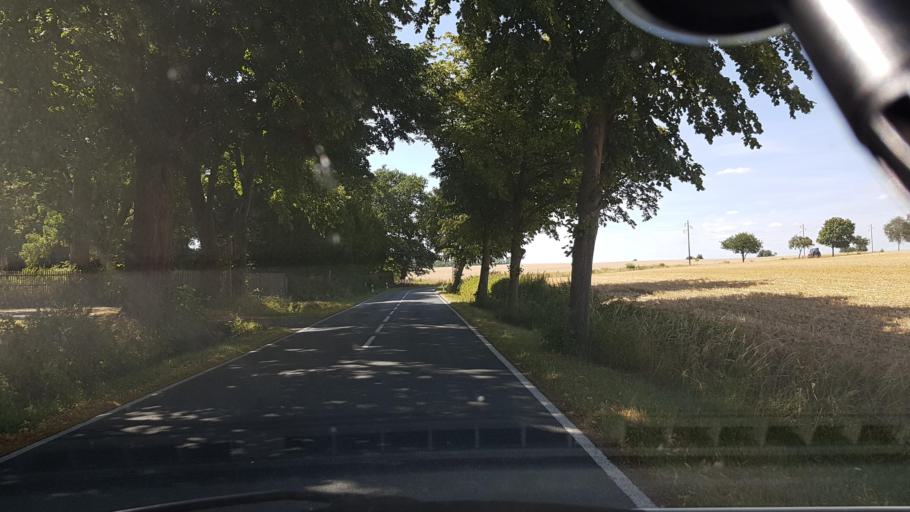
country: DE
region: Lower Saxony
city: Schoningen
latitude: 52.1618
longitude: 10.9612
